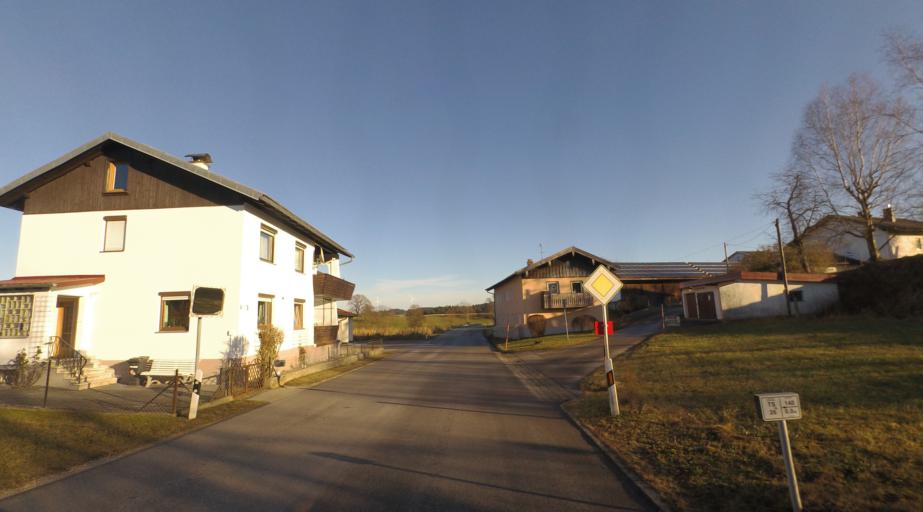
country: DE
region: Bavaria
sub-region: Upper Bavaria
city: Trostberg an der Alz
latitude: 48.0211
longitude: 12.5884
